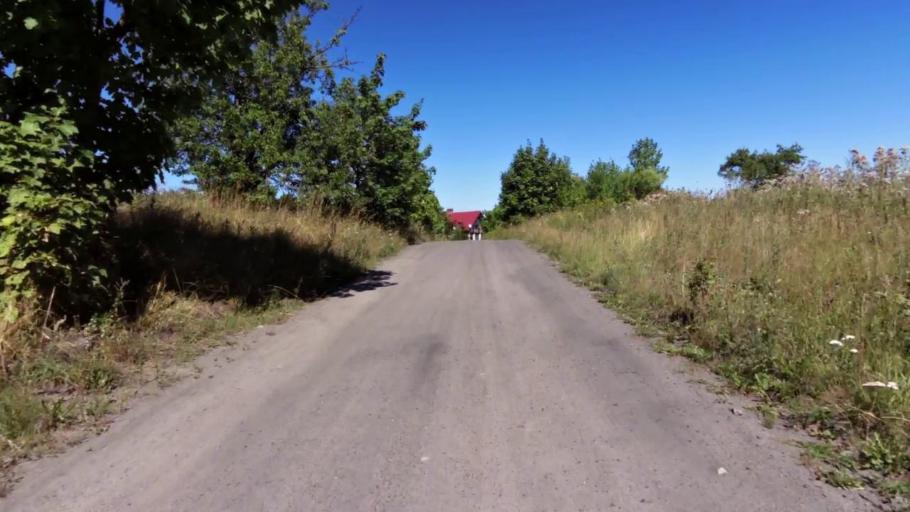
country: PL
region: West Pomeranian Voivodeship
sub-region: Powiat szczecinecki
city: Borne Sulinowo
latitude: 53.6713
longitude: 16.5640
